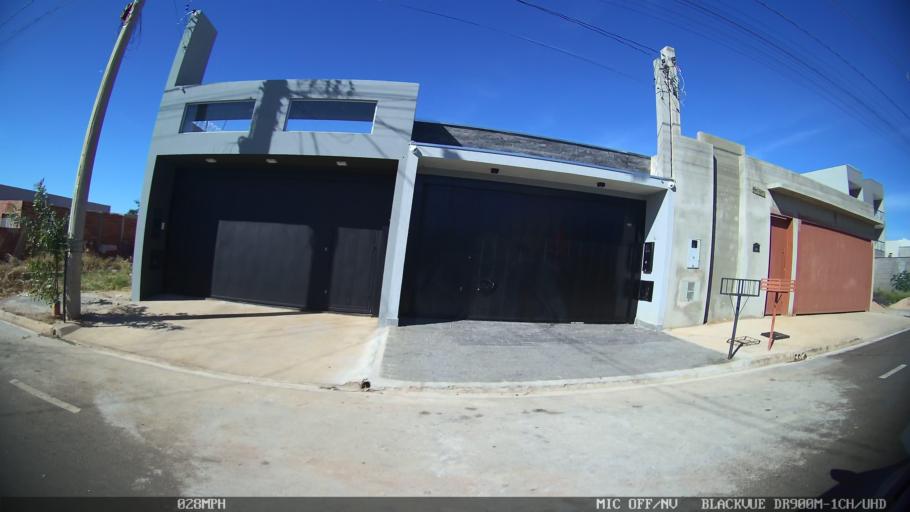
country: BR
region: Sao Paulo
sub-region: Franca
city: Franca
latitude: -20.5678
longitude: -47.3468
